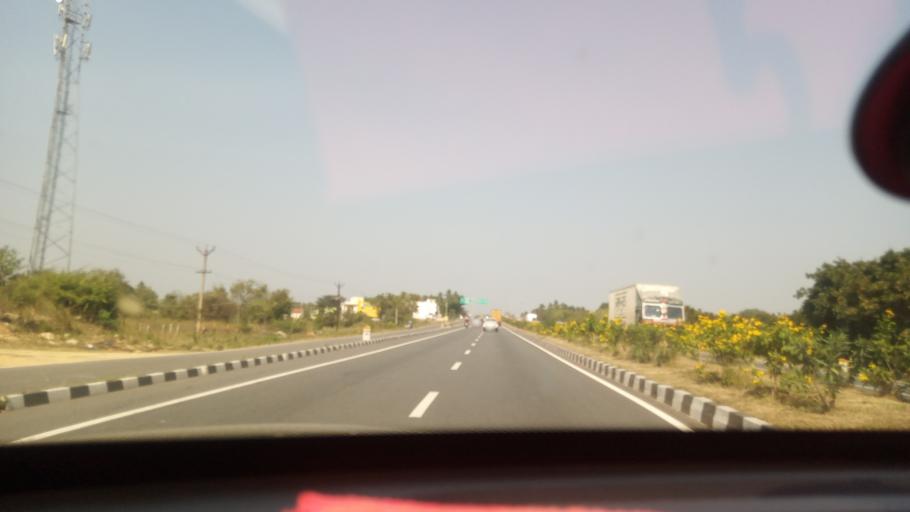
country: IN
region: Tamil Nadu
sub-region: Dharmapuri
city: Dharmapuri
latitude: 12.0978
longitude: 78.1198
